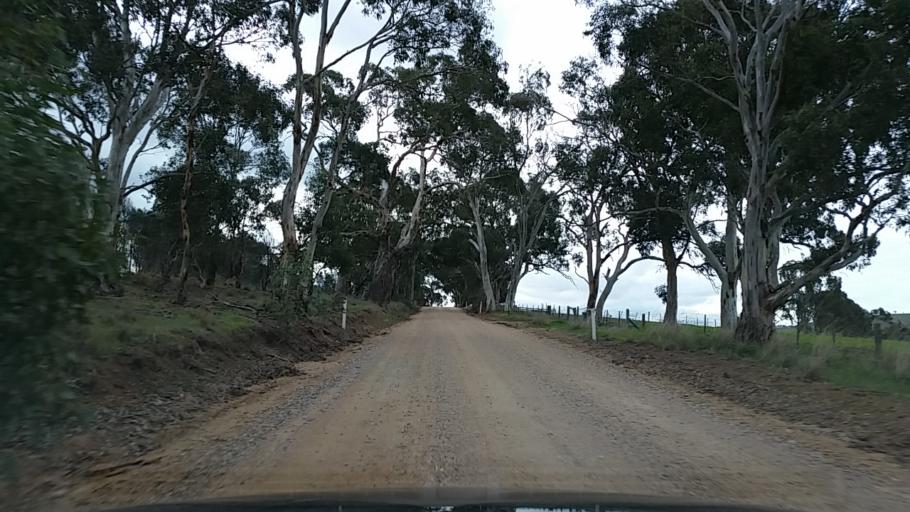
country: AU
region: South Australia
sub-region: Mount Barker
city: Nairne
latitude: -34.9638
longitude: 139.0237
